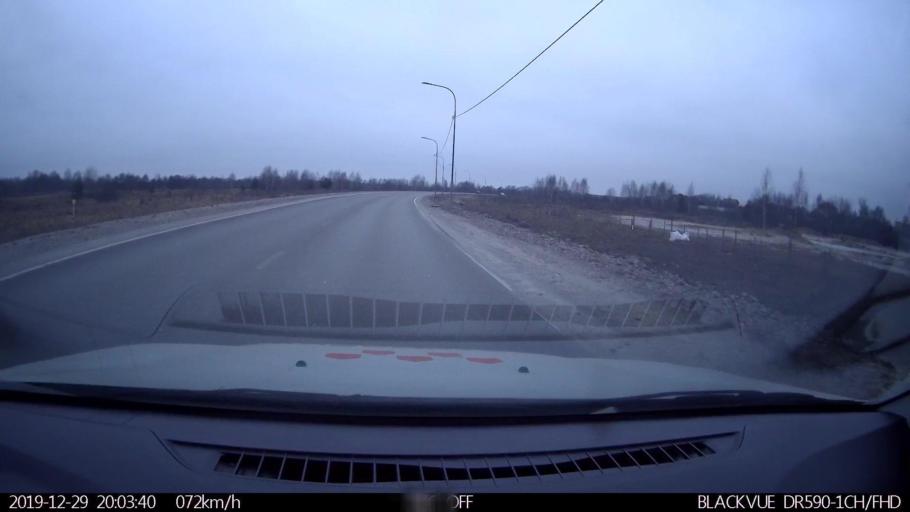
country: RU
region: Nizjnij Novgorod
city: Nizhniy Novgorod
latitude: 56.3756
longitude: 44.0146
